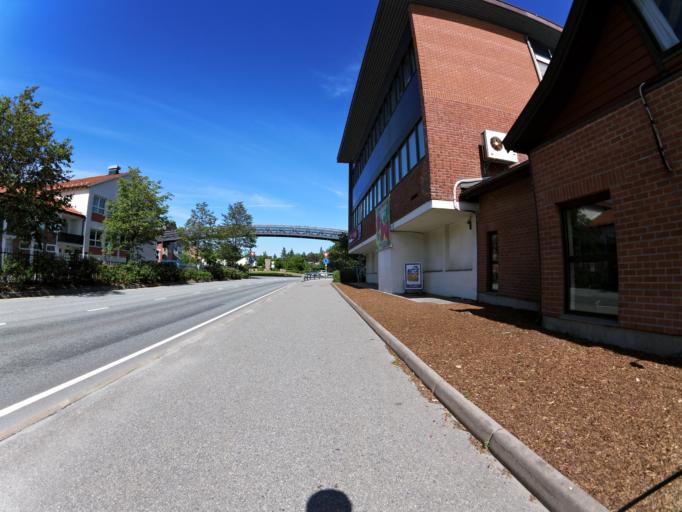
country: NO
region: Ostfold
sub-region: Fredrikstad
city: Fredrikstad
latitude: 59.2181
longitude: 10.9444
